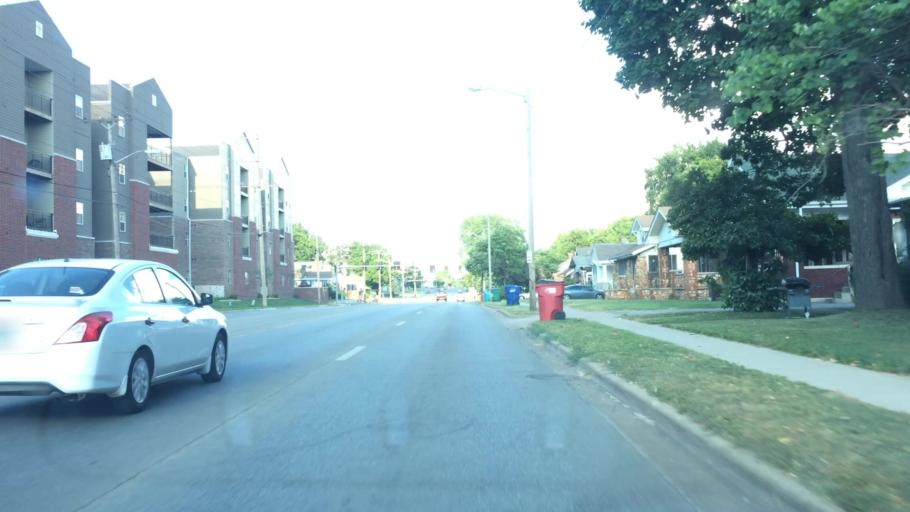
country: US
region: Missouri
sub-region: Greene County
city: Springfield
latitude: 37.1968
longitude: -93.2887
